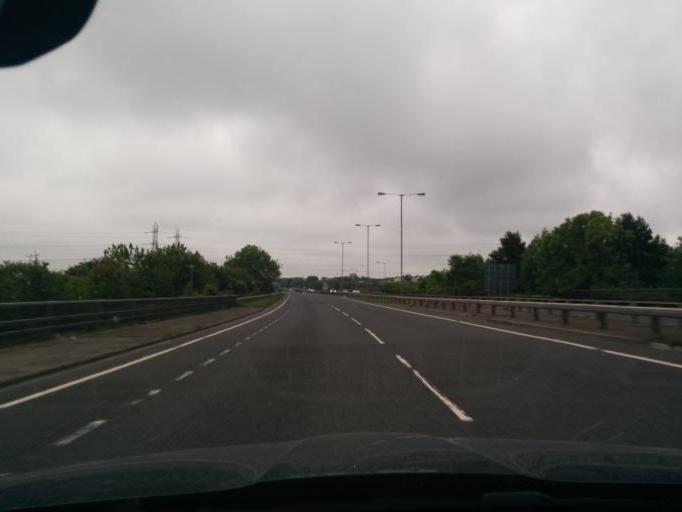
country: GB
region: England
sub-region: Northumberland
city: Bedlington
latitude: 55.1363
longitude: -1.5595
